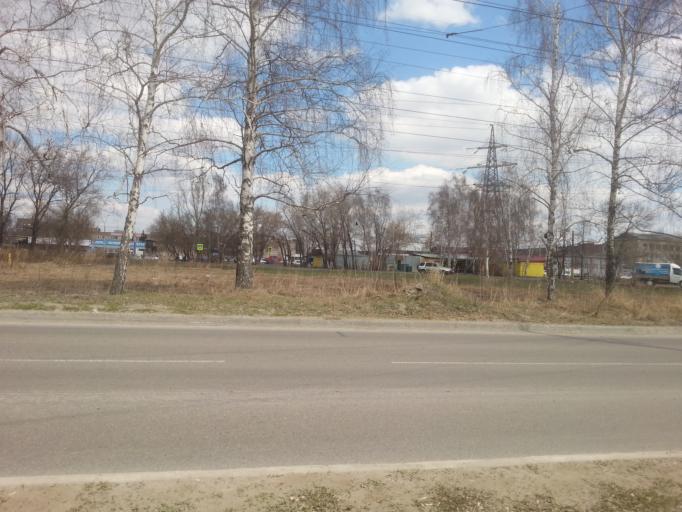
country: RU
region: Altai Krai
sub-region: Gorod Barnaulskiy
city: Barnaul
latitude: 53.3860
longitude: 83.7116
